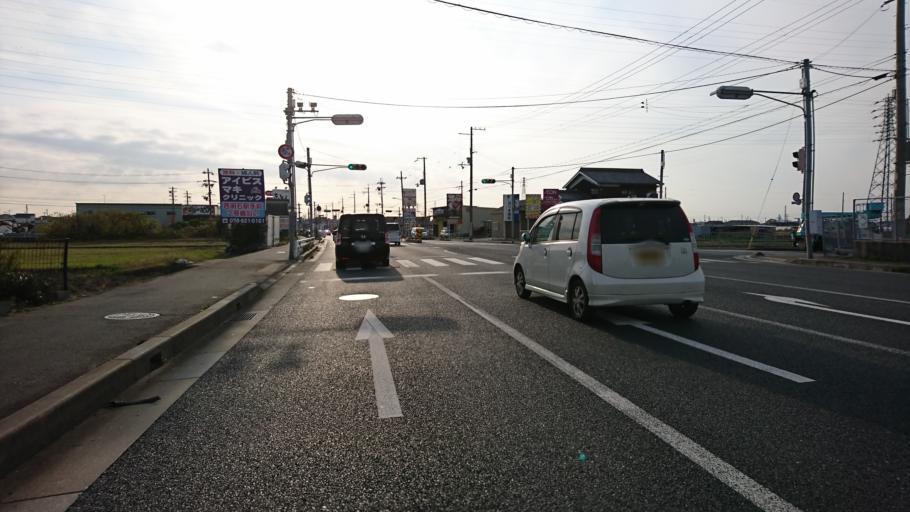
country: JP
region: Hyogo
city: Kakogawacho-honmachi
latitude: 34.7139
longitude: 134.8862
